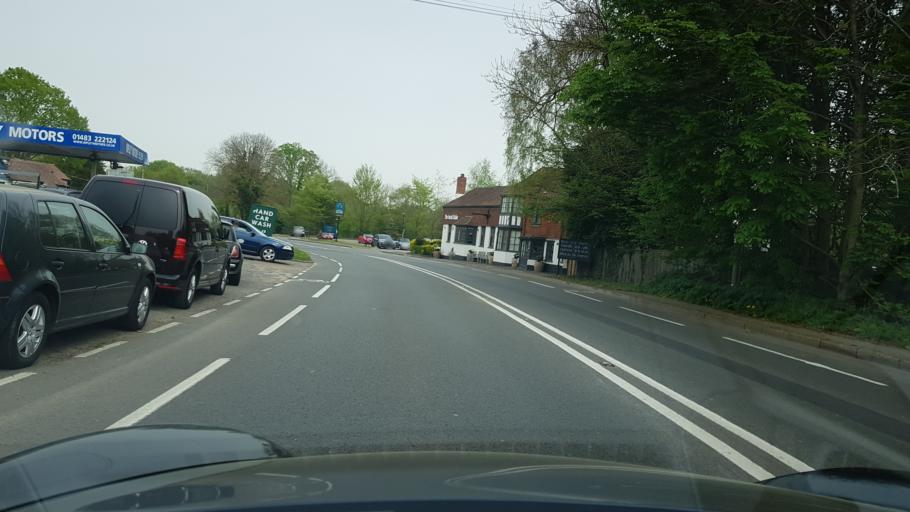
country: GB
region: England
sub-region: Surrey
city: Ripley
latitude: 51.2888
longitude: -0.5027
